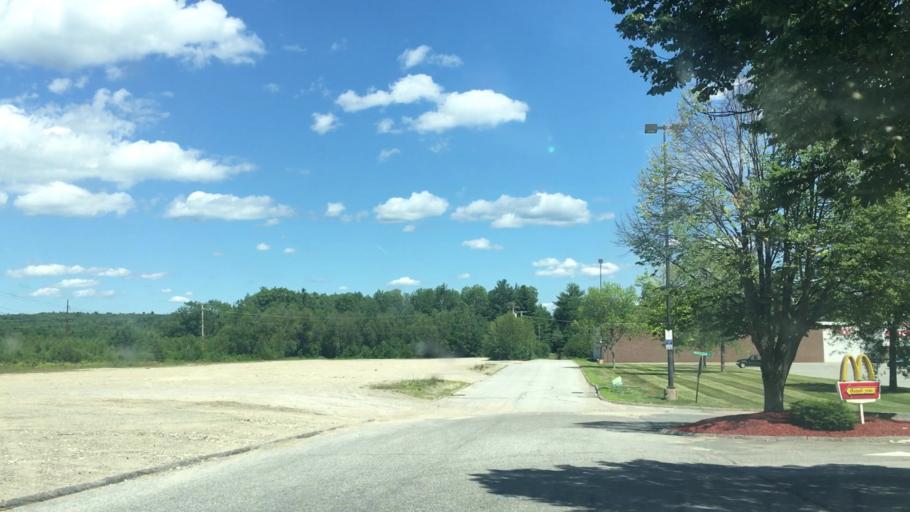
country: US
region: Maine
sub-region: Franklin County
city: Jay
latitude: 44.5068
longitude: -70.2170
